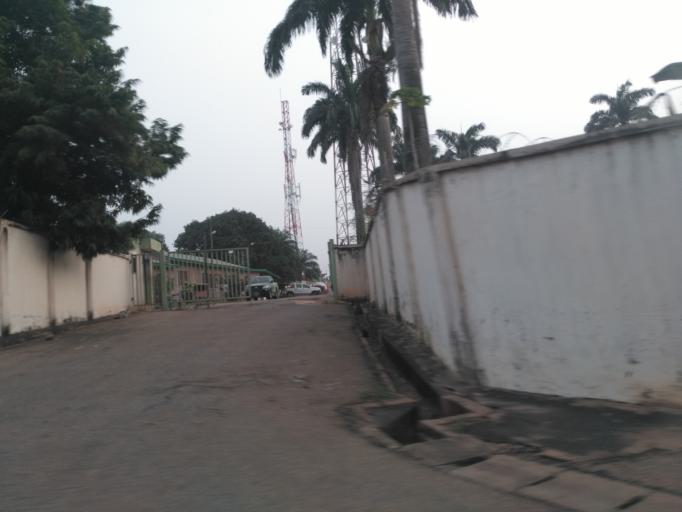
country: GH
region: Ashanti
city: Kumasi
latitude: 6.6831
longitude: -1.6192
